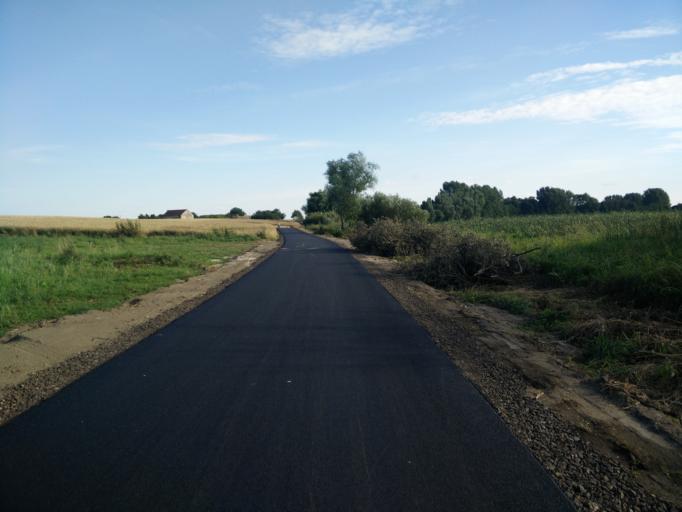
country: PL
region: Greater Poland Voivodeship
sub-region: Powiat sredzki
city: Sroda Wielkopolska
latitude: 52.2472
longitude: 17.2981
